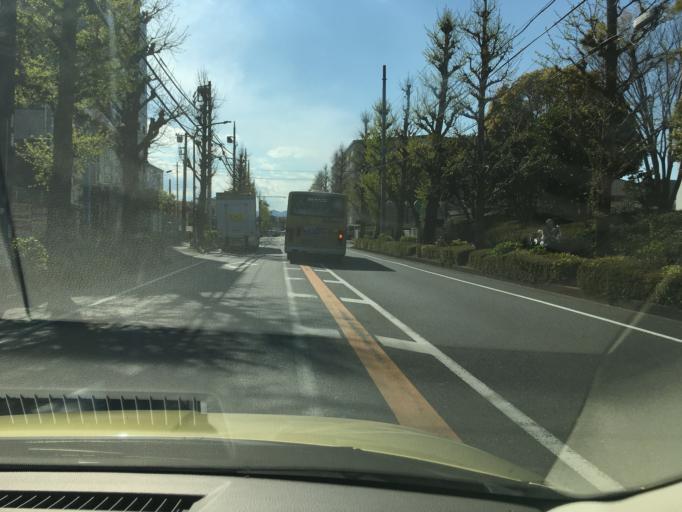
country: JP
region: Tokyo
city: Hachioji
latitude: 35.5763
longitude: 139.3514
